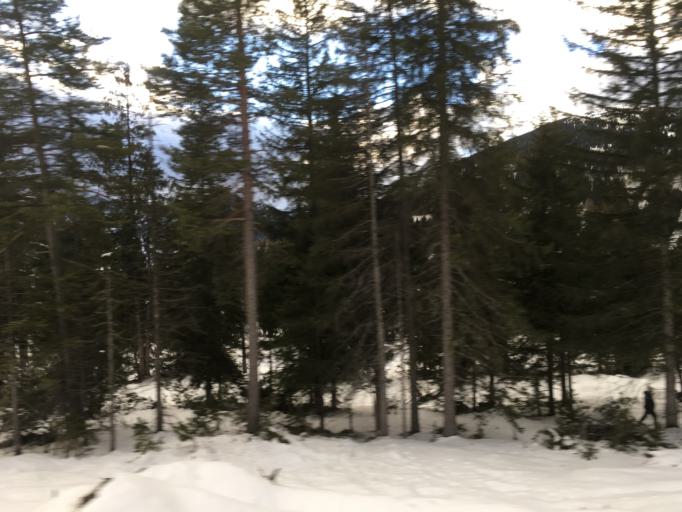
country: CH
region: Grisons
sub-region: Albula District
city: Tiefencastel
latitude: 46.7072
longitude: 9.5600
